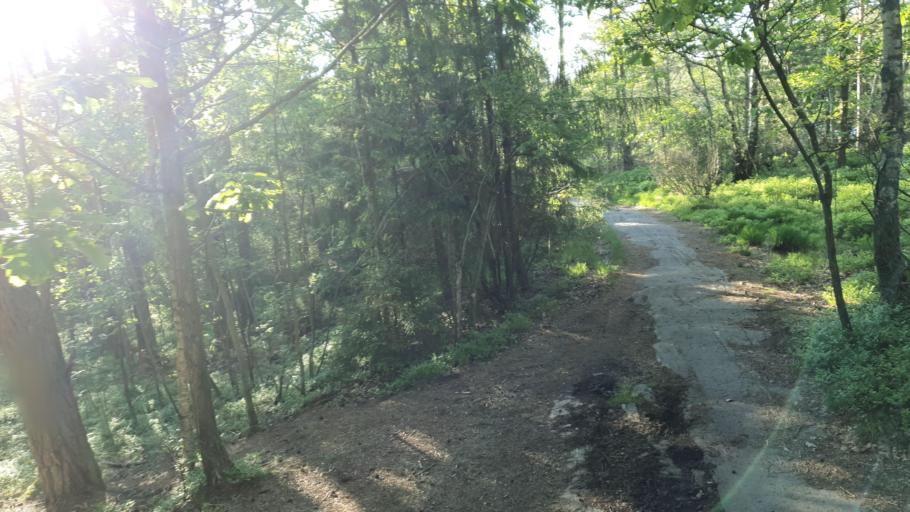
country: SE
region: Vaestra Goetaland
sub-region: Molndal
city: Kallered
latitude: 57.6376
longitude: 12.0530
